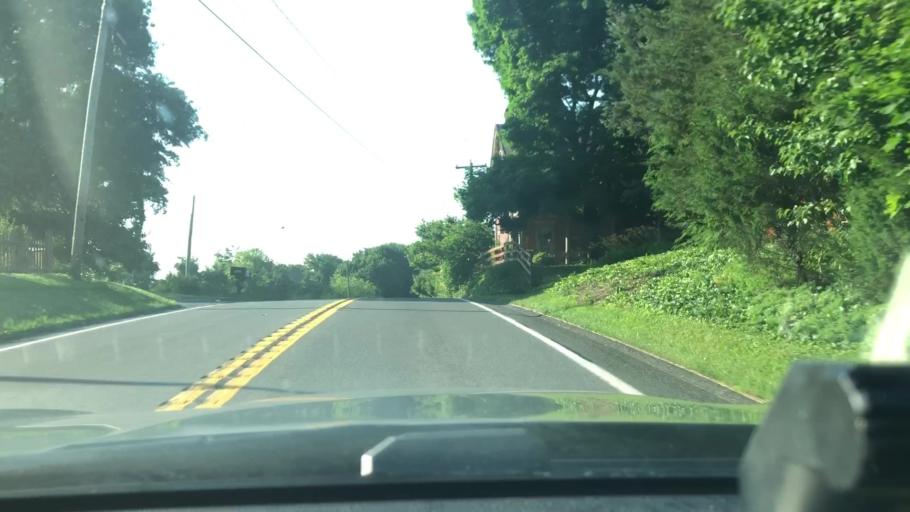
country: US
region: Pennsylvania
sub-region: Dauphin County
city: Palmdale
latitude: 40.3587
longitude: -76.6414
